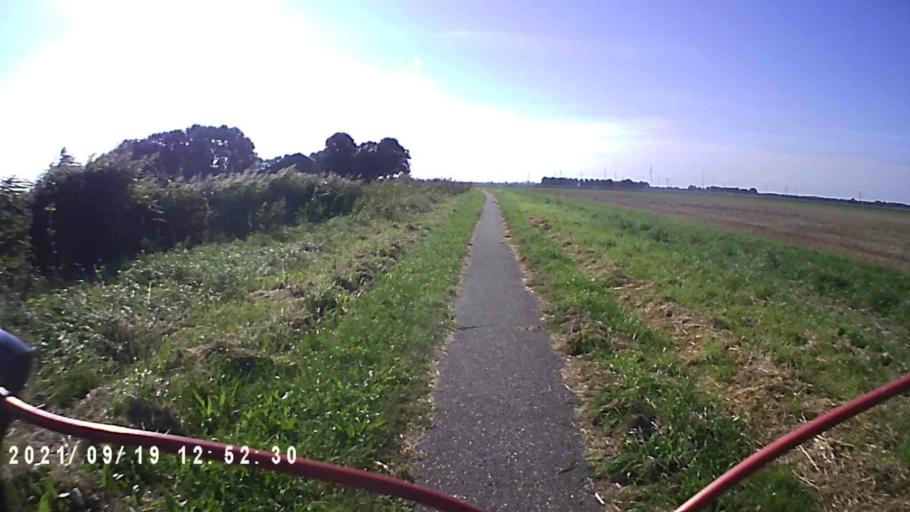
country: NL
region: Groningen
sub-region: Gemeente  Oldambt
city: Winschoten
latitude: 53.2058
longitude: 6.9478
